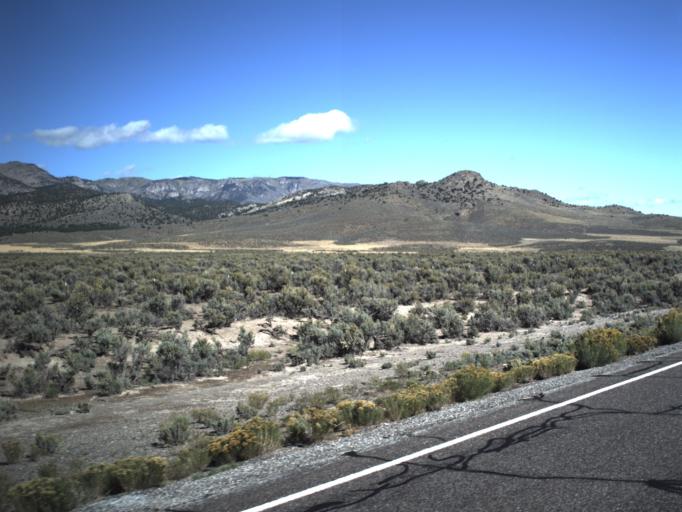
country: US
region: Utah
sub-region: Piute County
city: Junction
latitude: 38.2880
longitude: -111.9781
